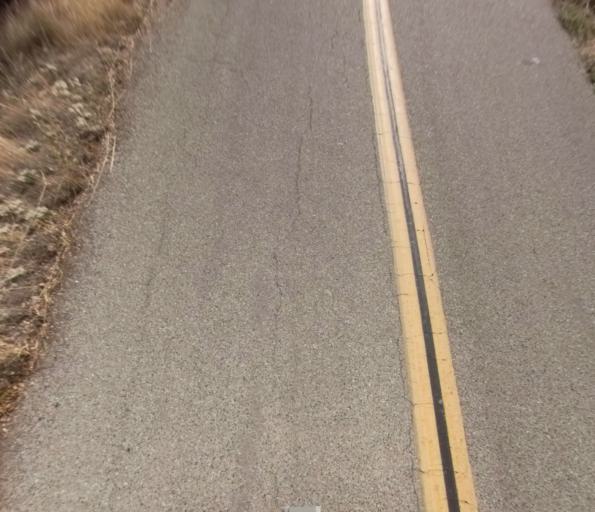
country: US
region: California
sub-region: Madera County
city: Yosemite Lakes
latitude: 37.2639
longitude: -119.9299
